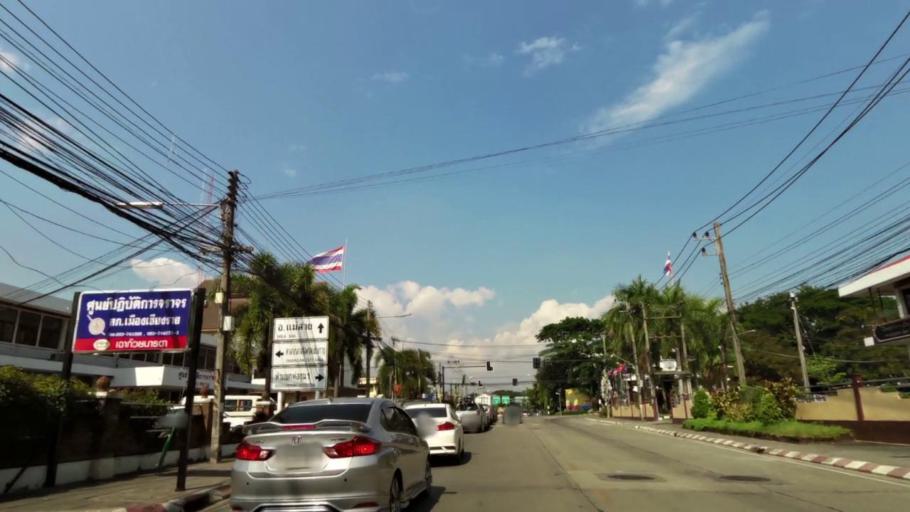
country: TH
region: Chiang Rai
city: Chiang Rai
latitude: 19.9121
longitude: 99.8326
